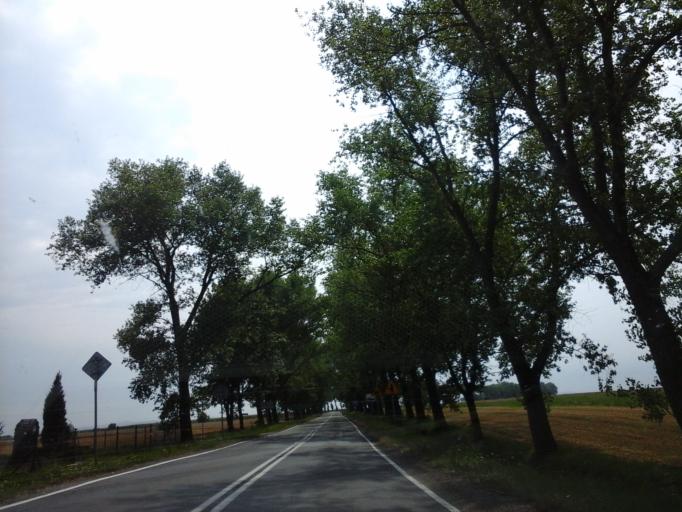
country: PL
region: Lower Silesian Voivodeship
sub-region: Powiat strzelinski
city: Strzelin
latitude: 50.8641
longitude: 17.0670
